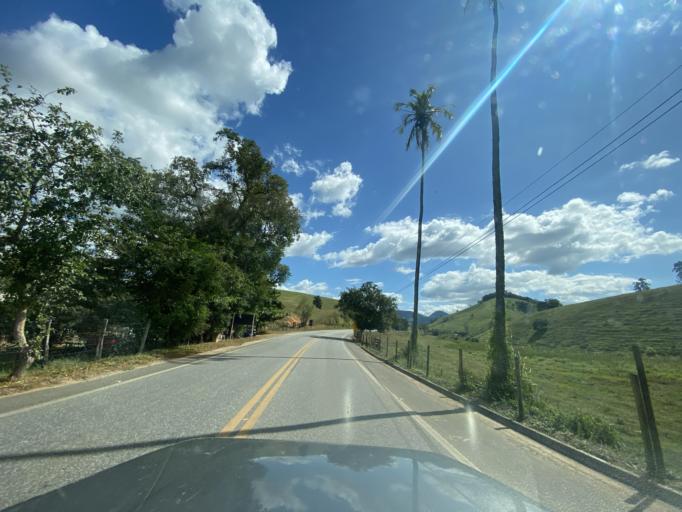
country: BR
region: Espirito Santo
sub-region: Jeronimo Monteiro
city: Jeronimo Monteiro
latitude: -20.7804
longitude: -41.4162
